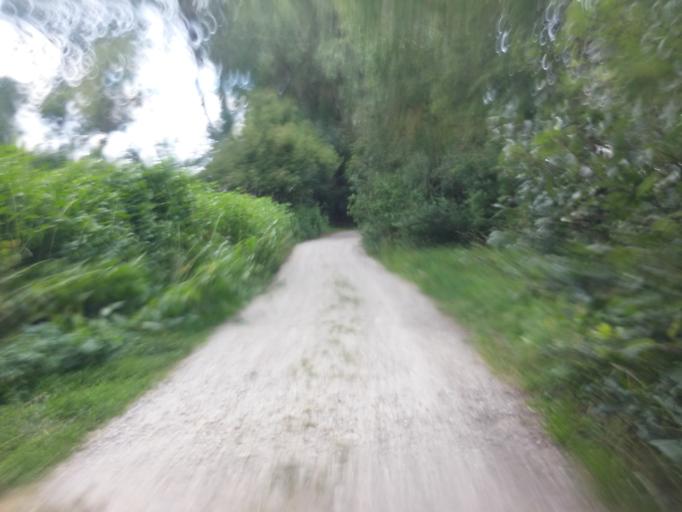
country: DE
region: Bavaria
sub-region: Upper Bavaria
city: Unterfoehring
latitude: 48.1708
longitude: 11.6765
